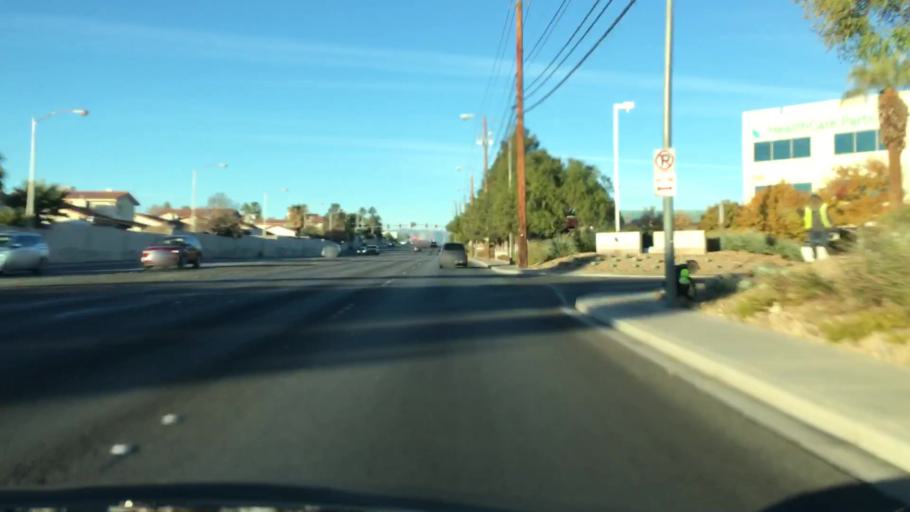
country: US
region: Nevada
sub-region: Clark County
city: Paradise
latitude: 36.0573
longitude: -115.1468
